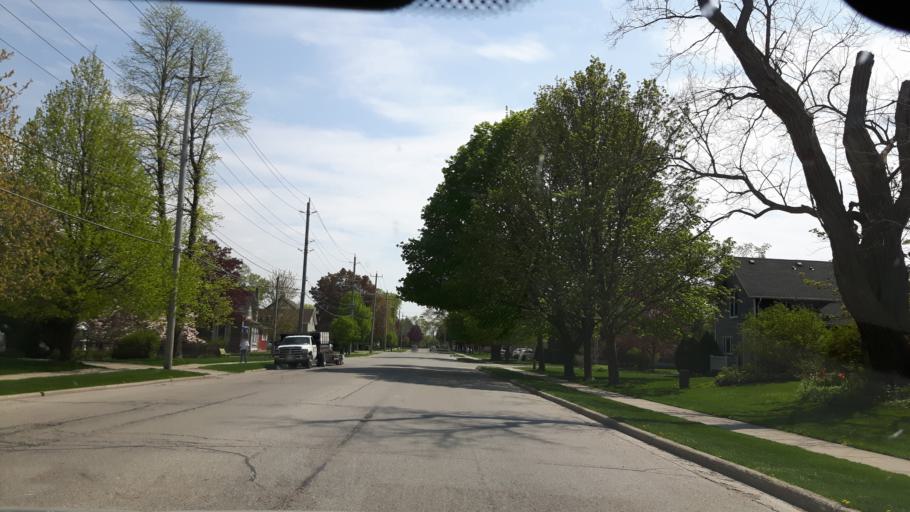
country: CA
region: Ontario
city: Goderich
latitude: 43.7420
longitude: -81.7179
